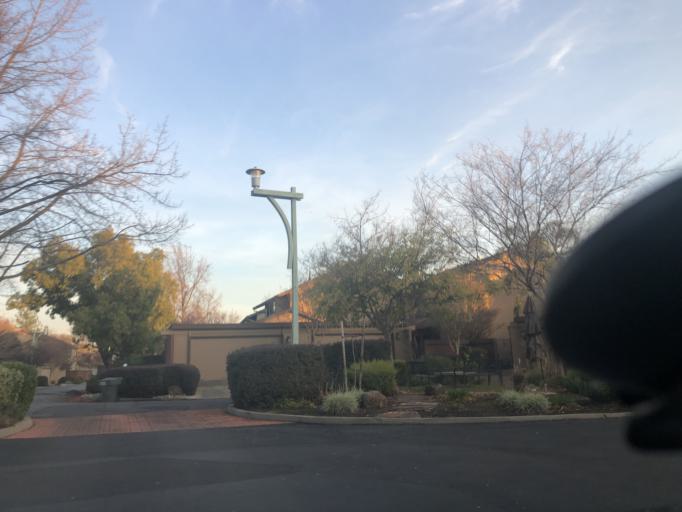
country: US
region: California
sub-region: Sacramento County
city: Gold River
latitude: 38.6370
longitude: -121.2304
